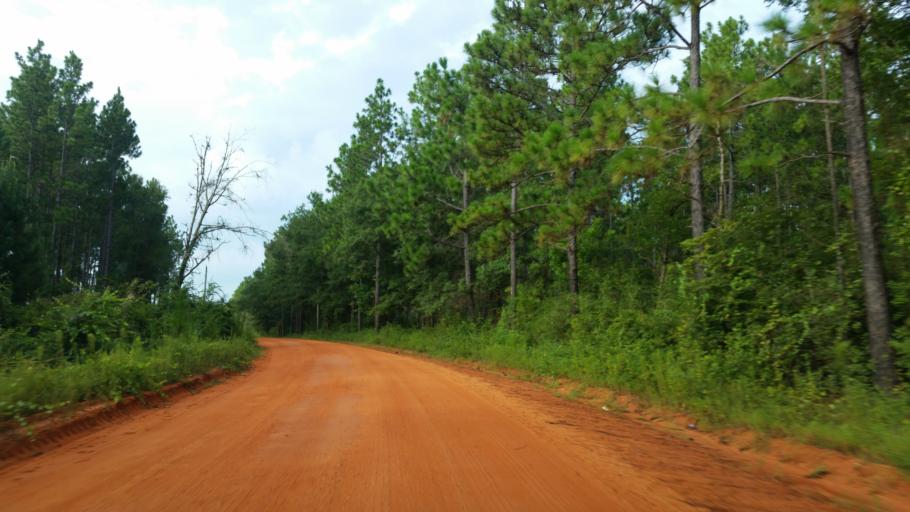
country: US
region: Alabama
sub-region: Escambia County
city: Atmore
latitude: 30.8970
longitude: -87.5832
